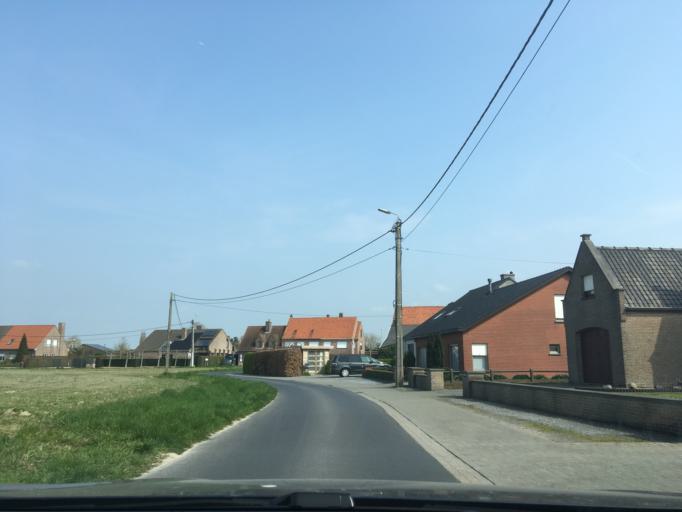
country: BE
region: Flanders
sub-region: Provincie West-Vlaanderen
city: Ardooie
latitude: 50.9831
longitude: 3.1940
